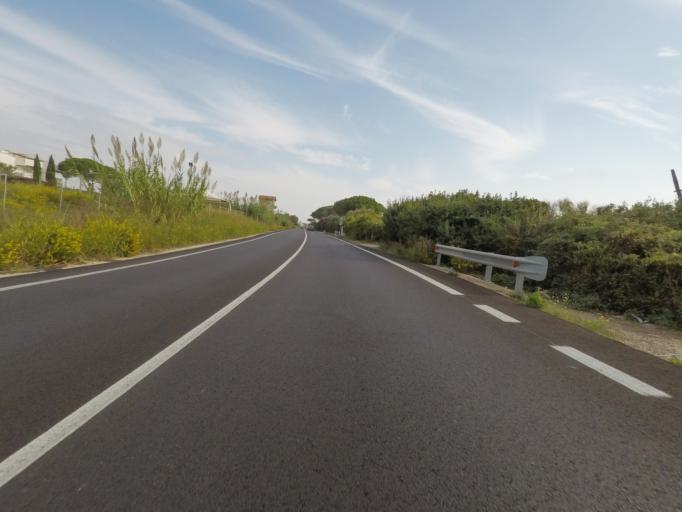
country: IT
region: Latium
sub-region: Citta metropolitana di Roma Capitale
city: Santa Marinella
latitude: 42.0481
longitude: 11.8214
